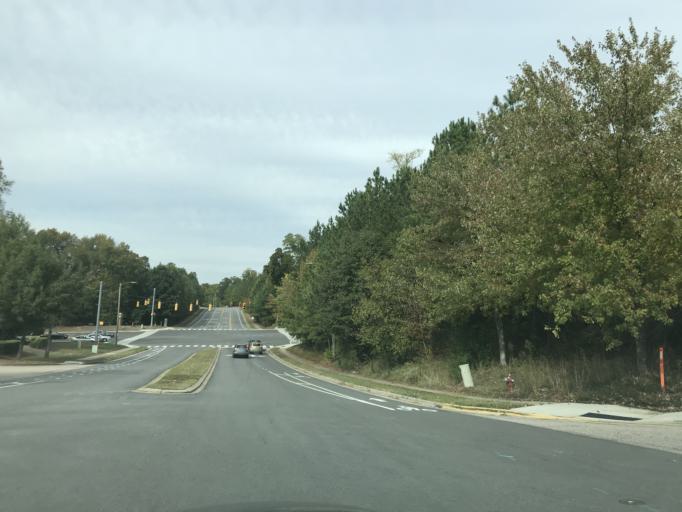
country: US
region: North Carolina
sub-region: Wake County
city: Wake Forest
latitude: 35.9447
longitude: -78.5449
